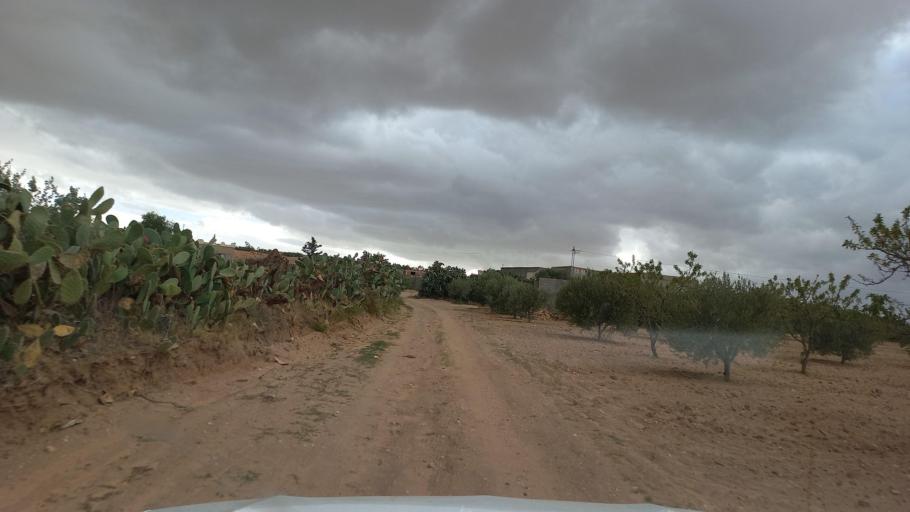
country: TN
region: Al Qasrayn
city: Kasserine
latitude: 35.2754
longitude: 8.9536
